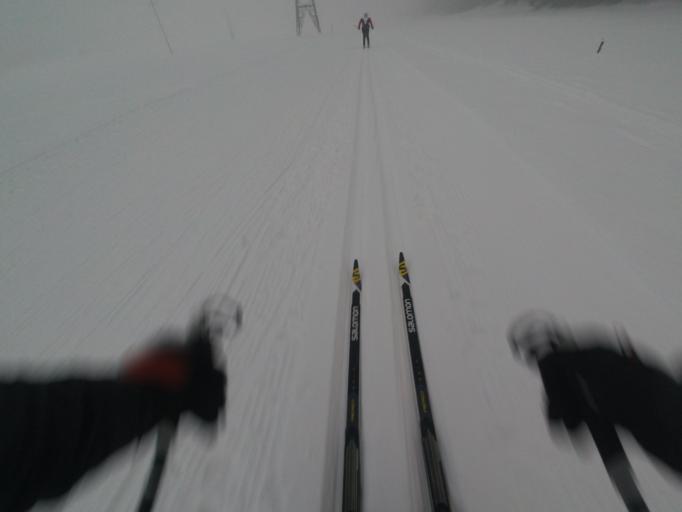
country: AT
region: Salzburg
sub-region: Politischer Bezirk Sankt Johann im Pongau
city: Wagrain
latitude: 47.3557
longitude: 13.3378
